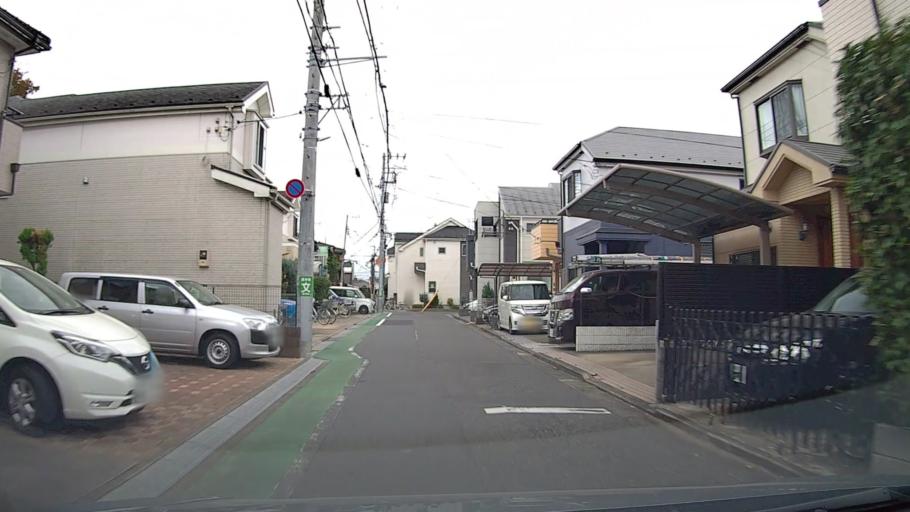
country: JP
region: Saitama
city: Wako
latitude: 35.7436
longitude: 139.6227
